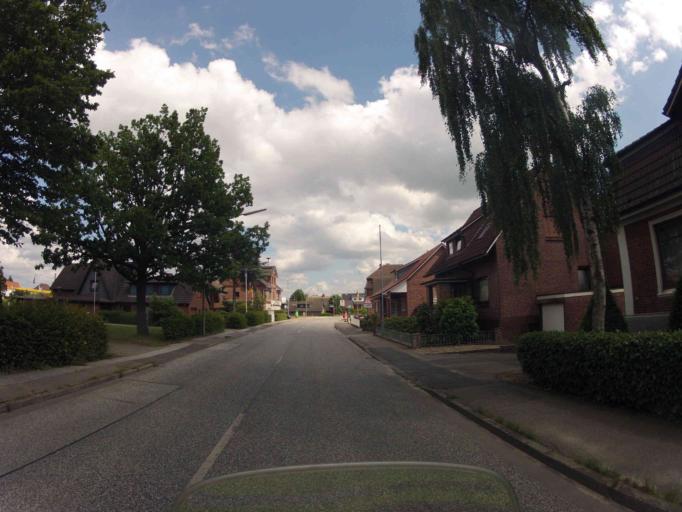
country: DE
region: Lower Saxony
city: Stelle
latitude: 53.4204
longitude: 10.1468
